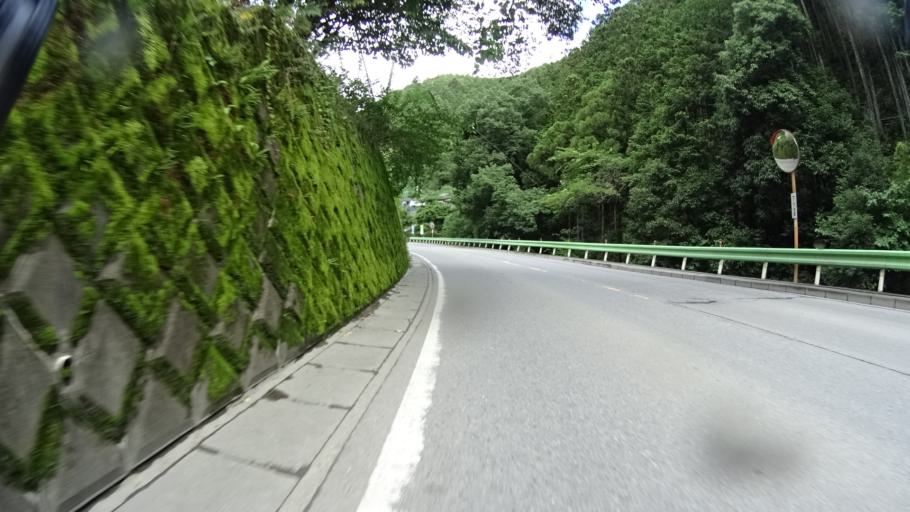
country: JP
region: Tokyo
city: Ome
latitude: 35.8242
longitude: 139.2263
